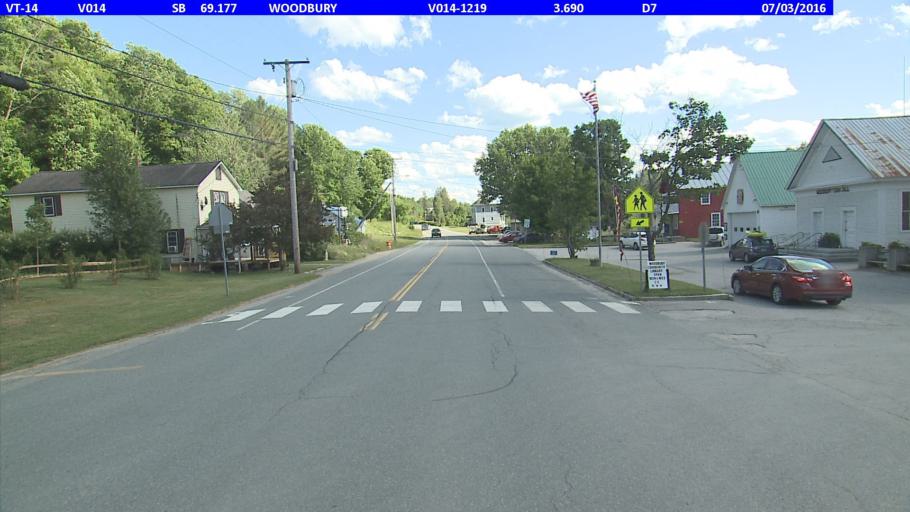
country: US
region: Vermont
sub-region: Caledonia County
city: Hardwick
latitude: 44.4411
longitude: -72.4152
